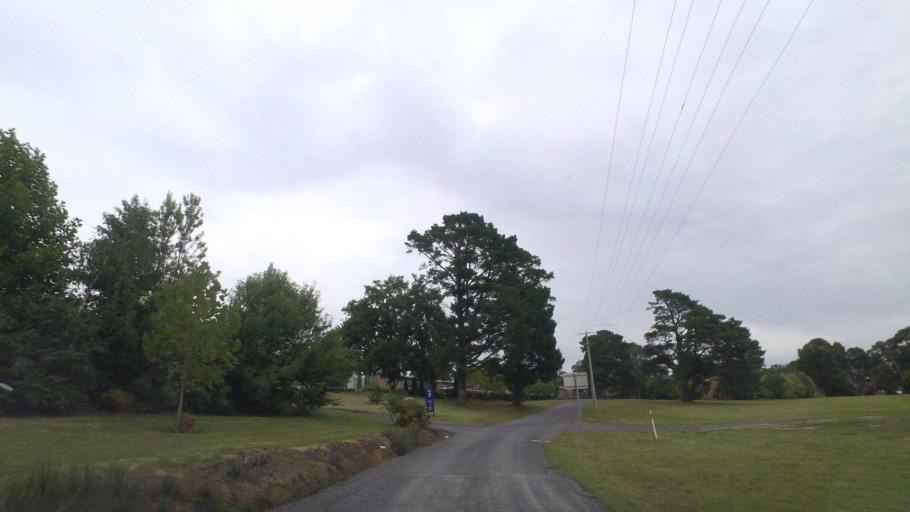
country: AU
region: Victoria
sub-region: Yarra Ranges
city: Mount Evelyn
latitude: -37.7830
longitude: 145.3515
